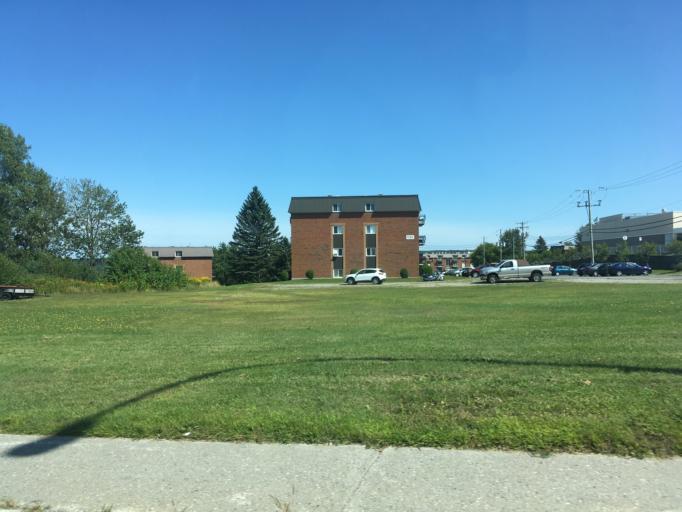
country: CA
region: Quebec
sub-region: Estrie
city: Sherbrooke
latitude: 45.4237
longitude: -71.8725
